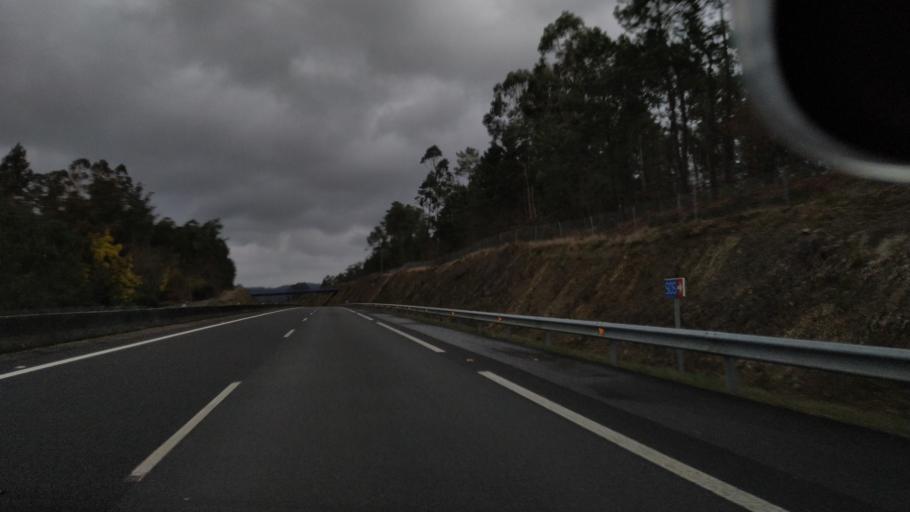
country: ES
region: Galicia
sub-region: Provincia da Coruna
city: Vedra
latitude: 42.8041
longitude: -8.4830
